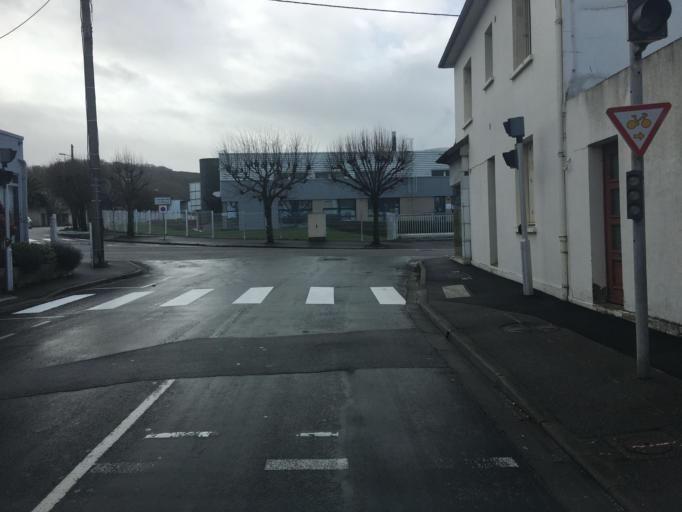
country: FR
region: Lower Normandy
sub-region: Departement de la Manche
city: Cherbourg-Octeville
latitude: 49.6332
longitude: -1.5985
